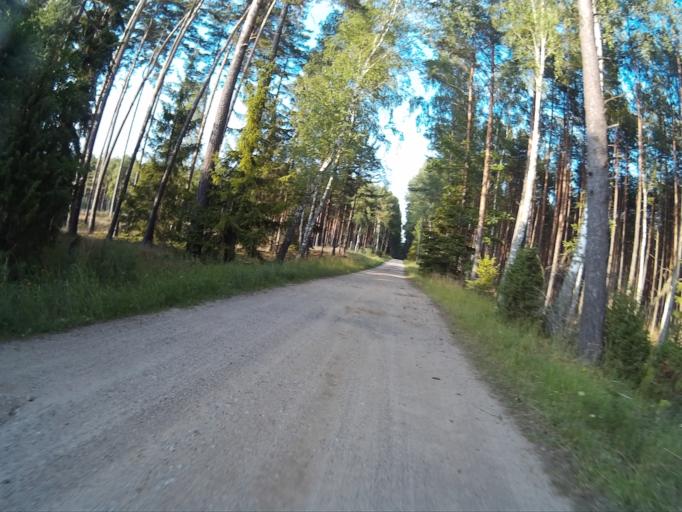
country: PL
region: Kujawsko-Pomorskie
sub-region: Powiat swiecki
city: Lniano
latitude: 53.5659
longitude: 18.1407
